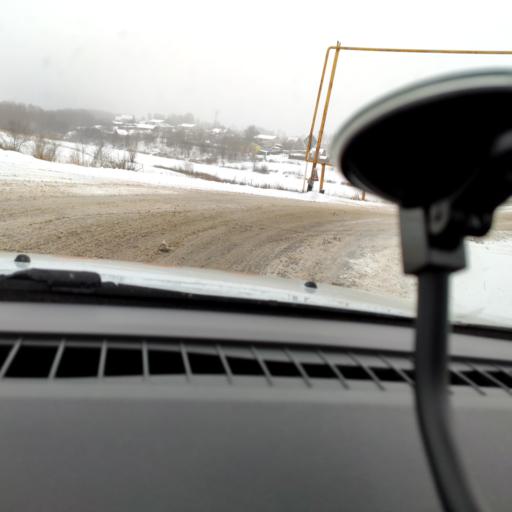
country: RU
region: Samara
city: Dubovyy Umet
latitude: 53.0411
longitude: 50.2425
